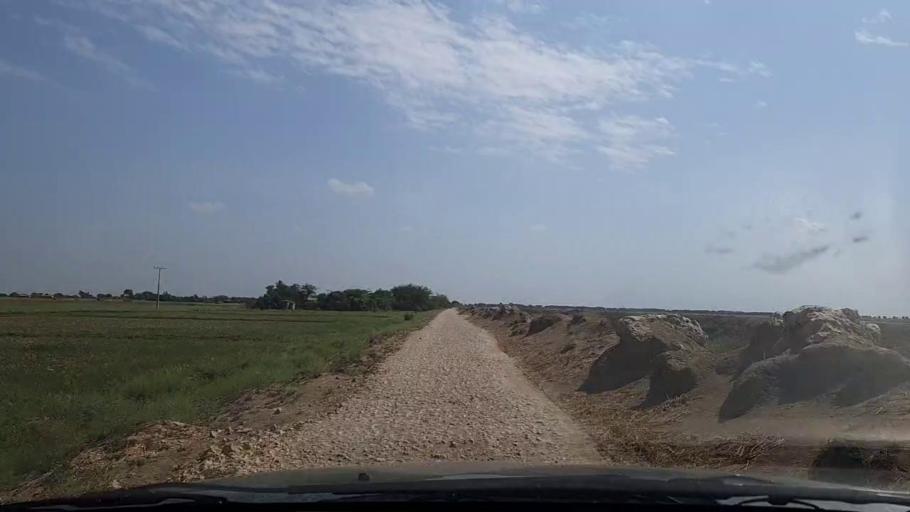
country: PK
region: Sindh
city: Mirpur Batoro
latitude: 24.5762
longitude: 68.1963
